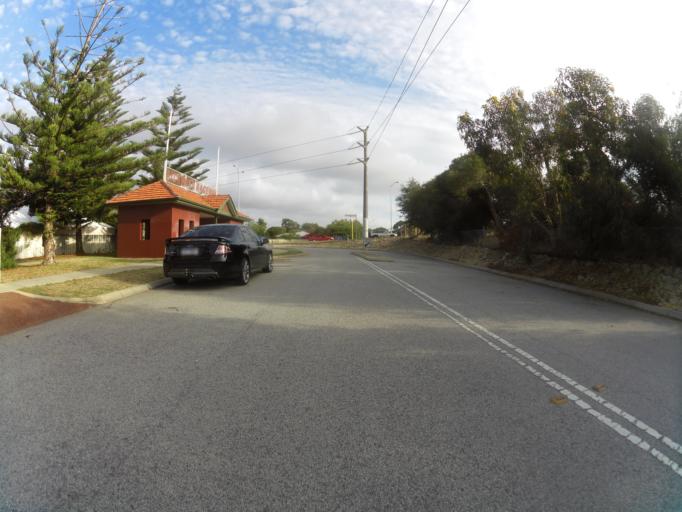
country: AU
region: Western Australia
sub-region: Fremantle
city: Fremantle
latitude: -32.0467
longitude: 115.7645
